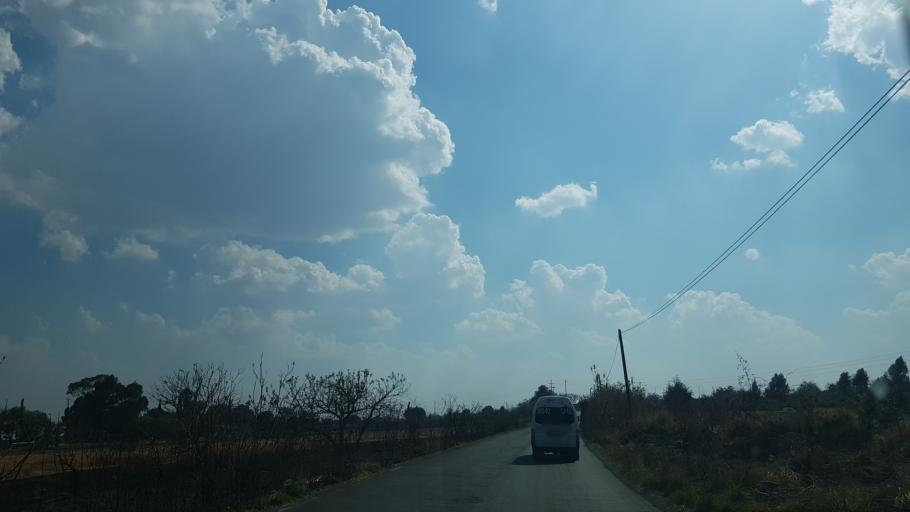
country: MX
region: Puebla
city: Atlixco
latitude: 18.9091
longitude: -98.4748
